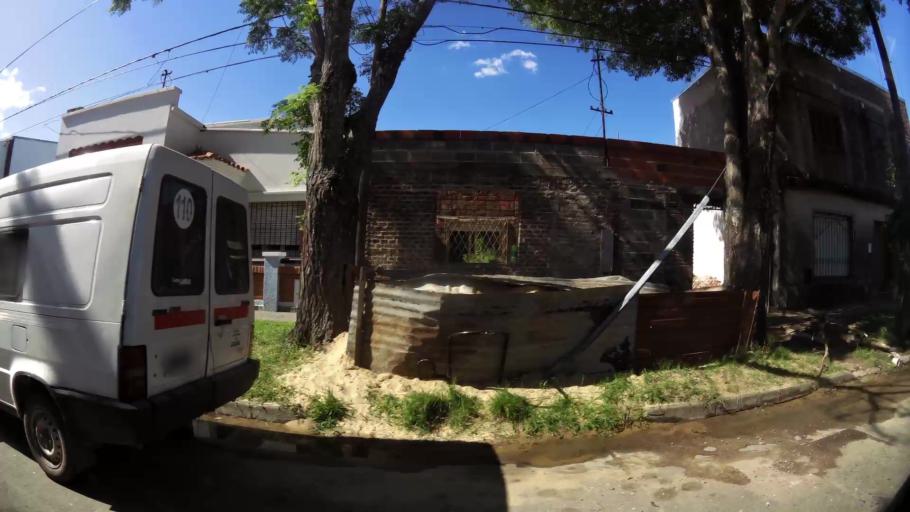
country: AR
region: Santa Fe
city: Santa Fe de la Vera Cruz
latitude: -31.6143
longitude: -60.6801
